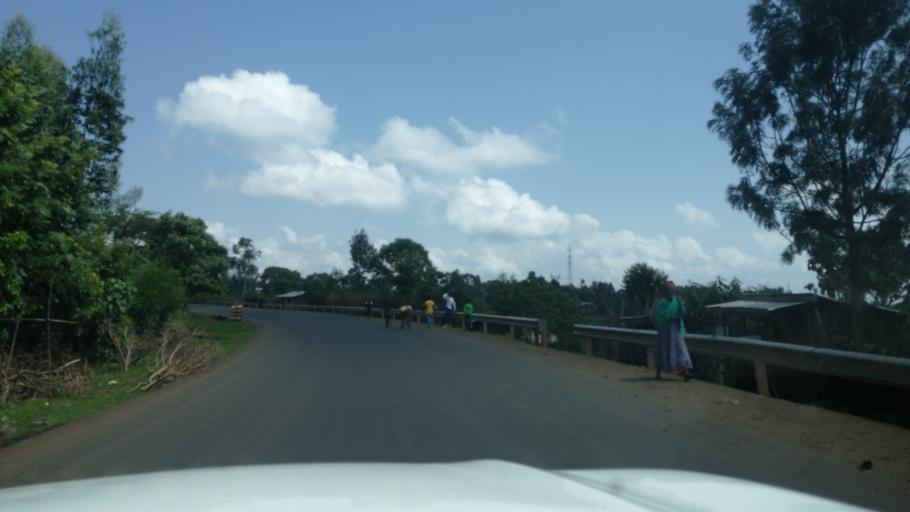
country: ET
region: Oromiya
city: Gedo
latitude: 8.9817
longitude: 37.5975
